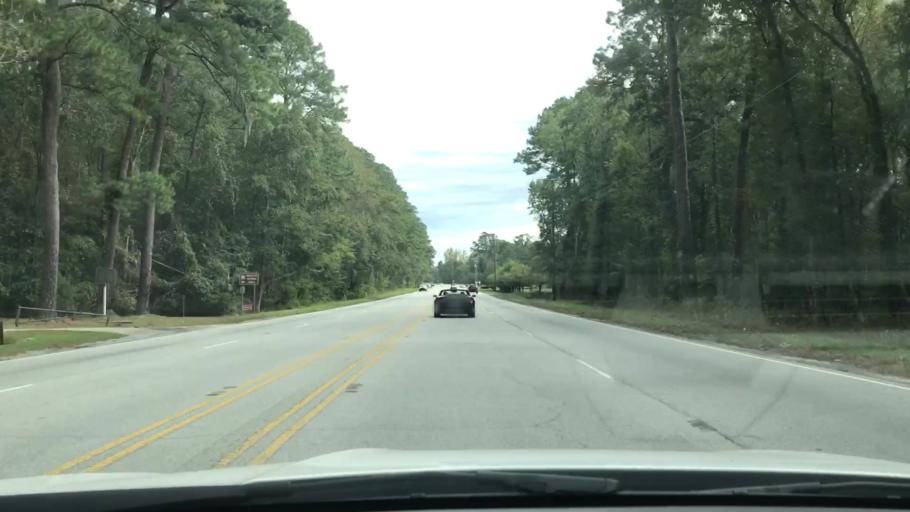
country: US
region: South Carolina
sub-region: Charleston County
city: Ravenel
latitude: 32.7690
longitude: -80.4528
